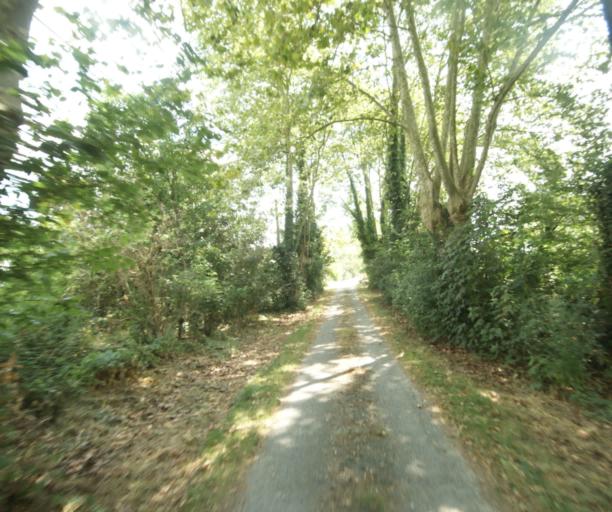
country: FR
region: Midi-Pyrenees
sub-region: Departement de la Haute-Garonne
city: Revel
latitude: 43.4349
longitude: 1.9764
